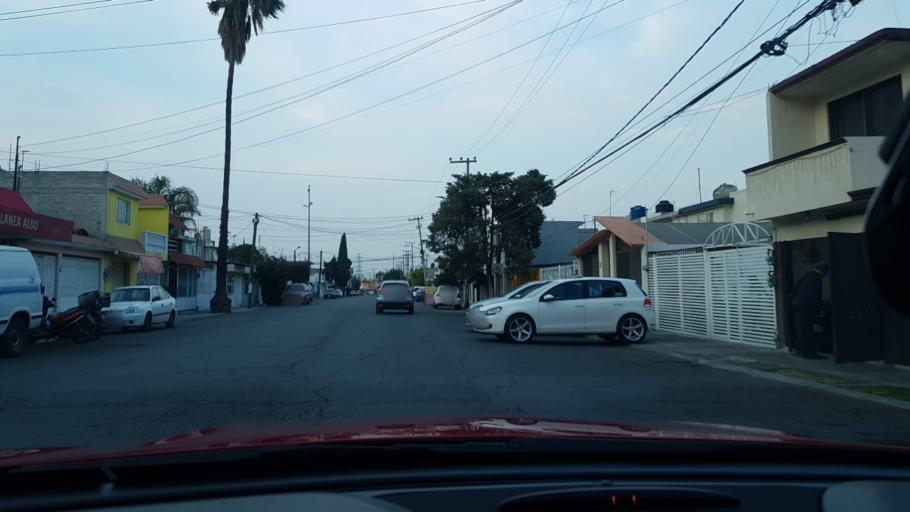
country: MX
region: Mexico
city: Cuautitlan
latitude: 19.6869
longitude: -99.2065
